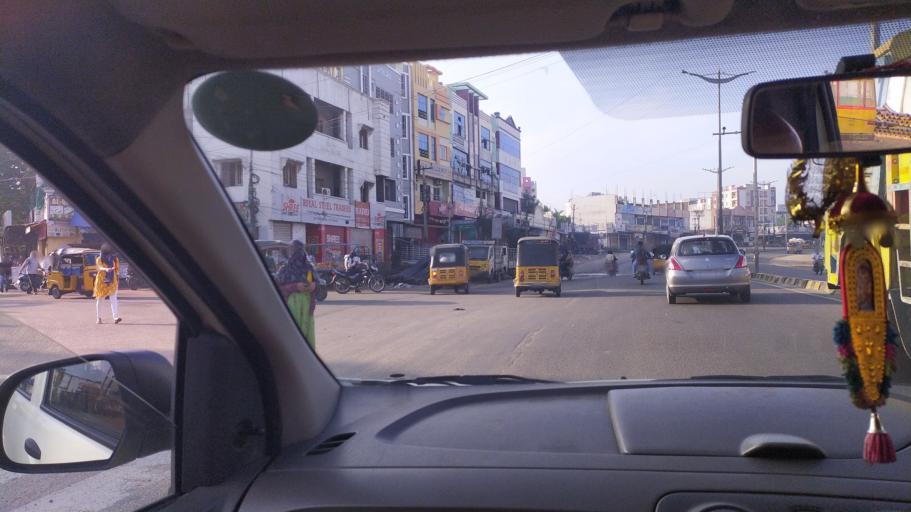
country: IN
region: Telangana
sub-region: Rangareddi
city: Balapur
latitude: 17.3168
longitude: 78.4664
